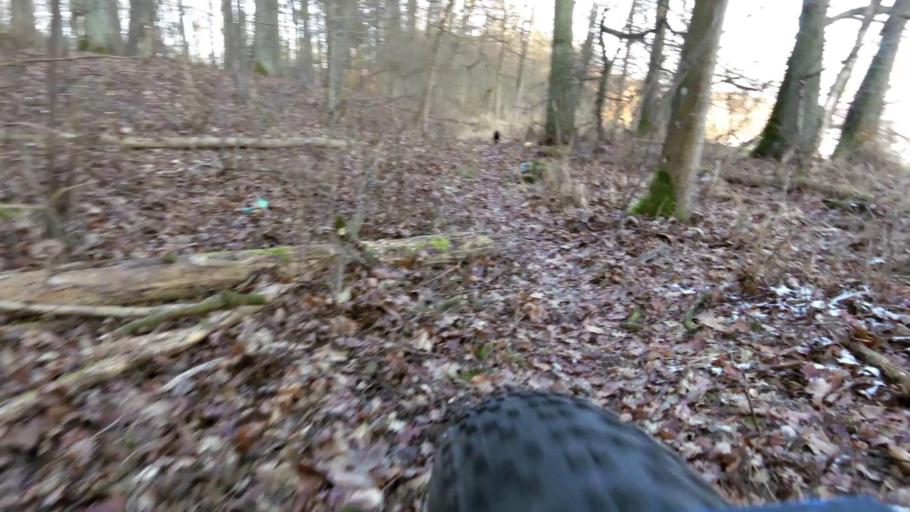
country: PL
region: West Pomeranian Voivodeship
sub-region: Powiat walecki
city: Walcz
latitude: 53.2513
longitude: 16.3794
